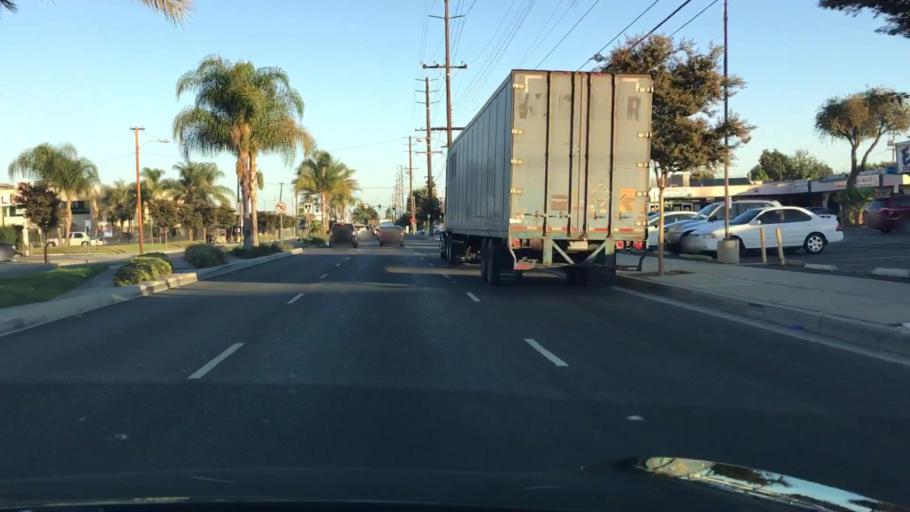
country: US
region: California
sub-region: Los Angeles County
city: Pico Rivera
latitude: 33.9597
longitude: -118.1083
